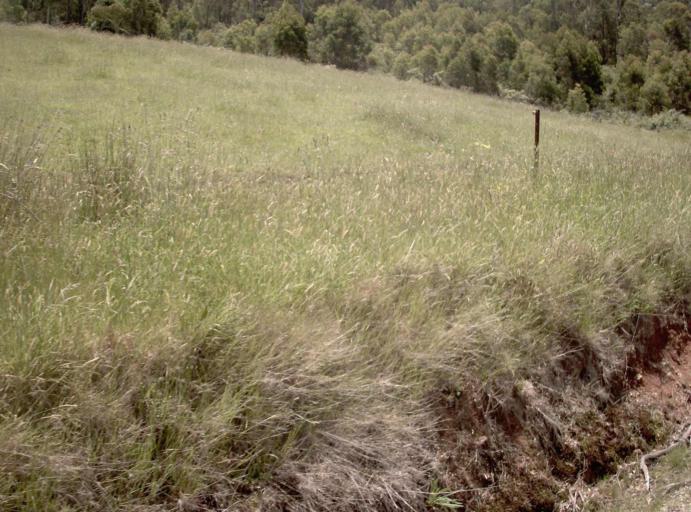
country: AU
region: New South Wales
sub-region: Bombala
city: Bombala
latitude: -37.3713
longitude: 149.0155
